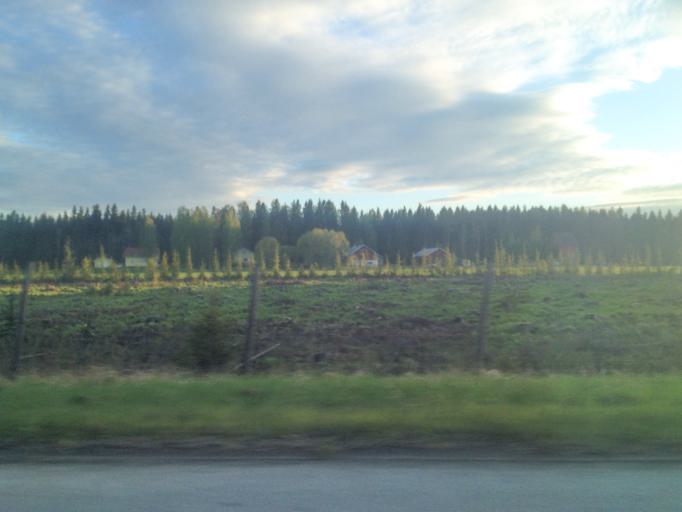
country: FI
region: Haeme
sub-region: Riihimaeki
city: Riihimaeki
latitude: 60.7789
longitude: 24.7096
